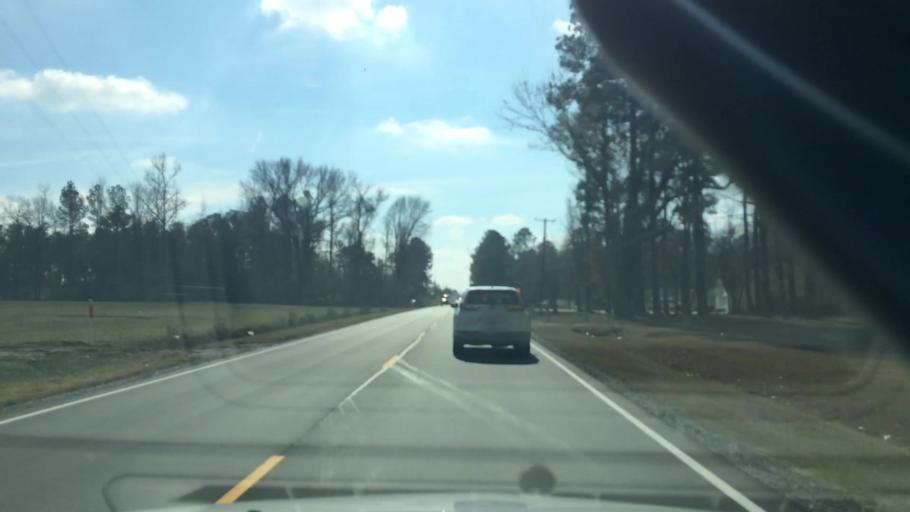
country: US
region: North Carolina
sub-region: Duplin County
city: Beulaville
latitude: 34.9353
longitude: -77.7708
